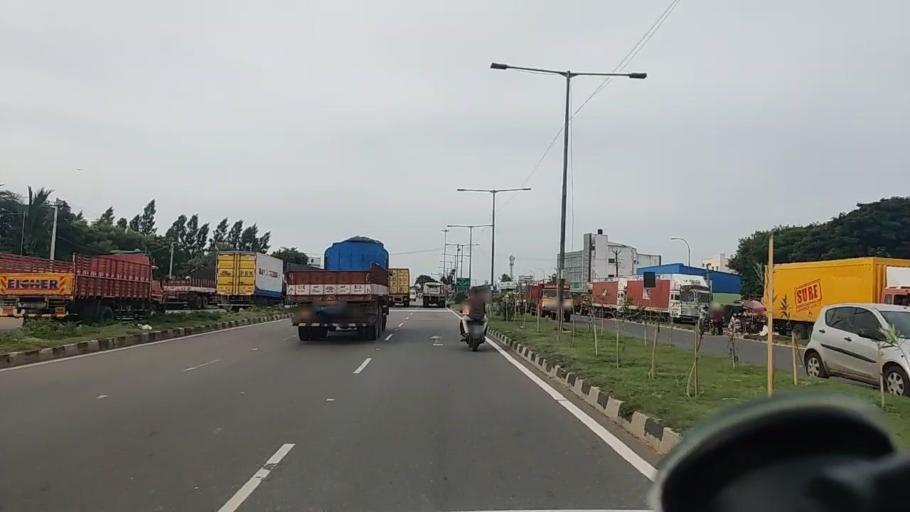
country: IN
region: Tamil Nadu
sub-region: Thiruvallur
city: Chinnasekkadu
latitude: 13.1567
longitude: 80.2251
